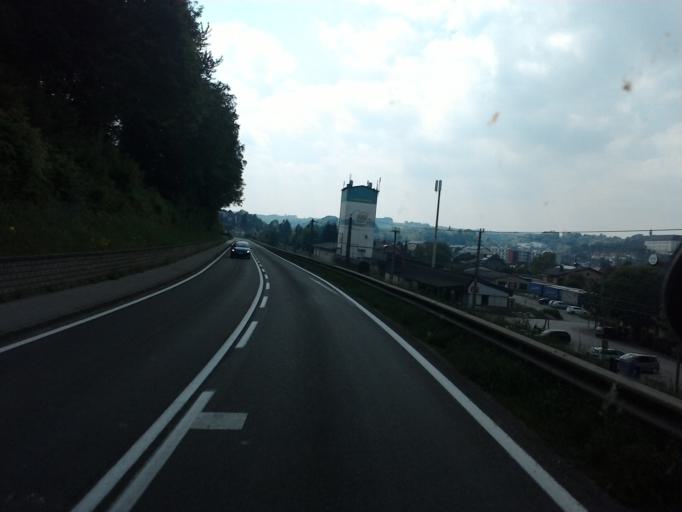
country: AT
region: Upper Austria
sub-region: Politischer Bezirk Kirchdorf an der Krems
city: Kremsmunster
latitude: 48.0533
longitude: 14.1413
